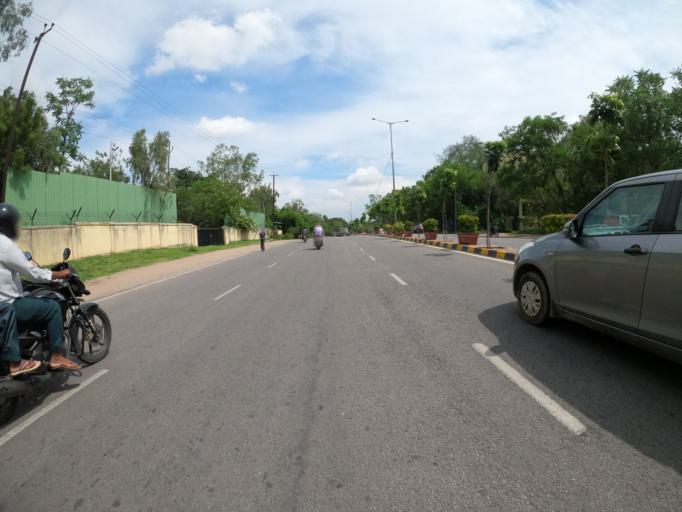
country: IN
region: Telangana
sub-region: Hyderabad
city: Hyderabad
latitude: 17.3844
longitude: 78.4226
